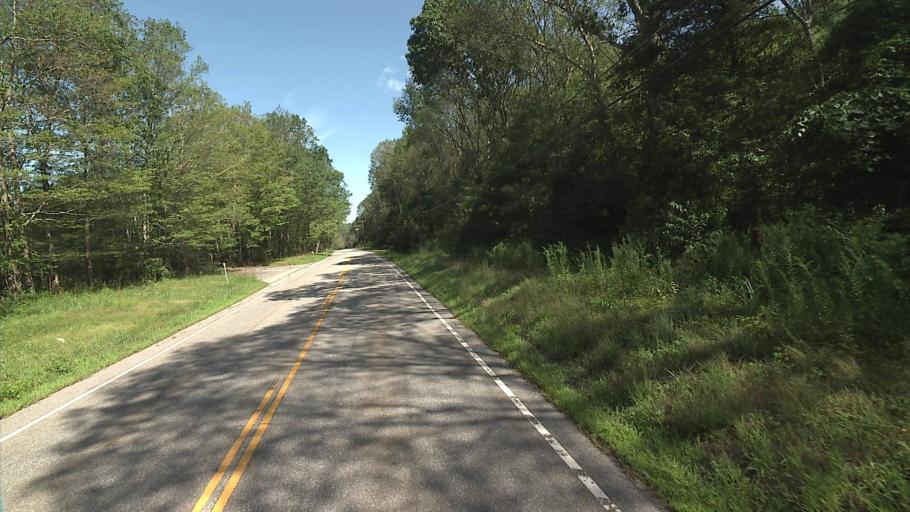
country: US
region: Connecticut
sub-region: New London County
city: Baltic
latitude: 41.6815
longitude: -72.0847
